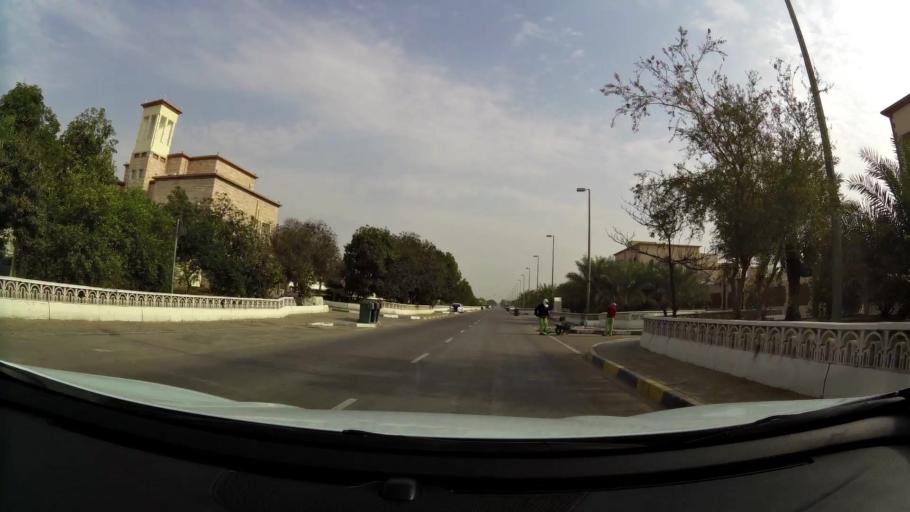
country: AE
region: Abu Dhabi
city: Abu Dhabi
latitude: 24.6678
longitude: 54.7516
